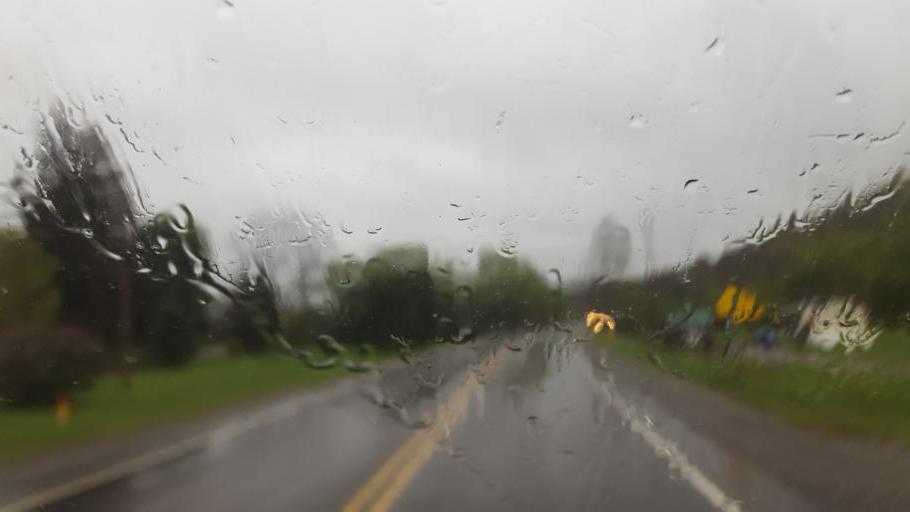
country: US
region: Pennsylvania
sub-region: Tioga County
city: Westfield
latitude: 41.9180
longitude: -77.5618
